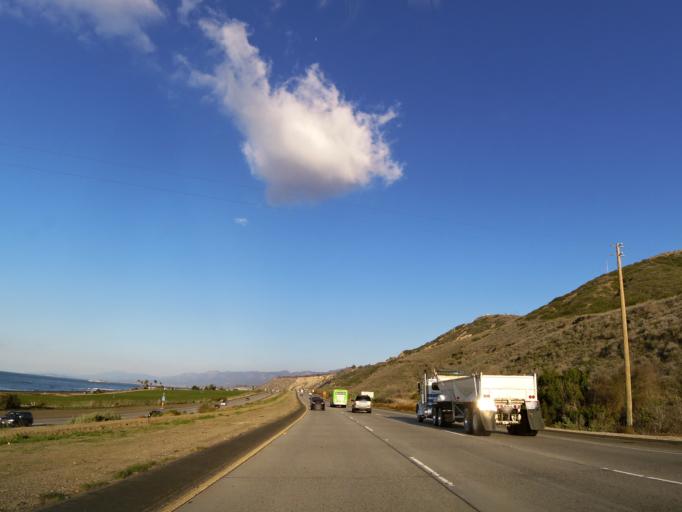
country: US
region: California
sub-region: Ventura County
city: Oak View
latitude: 34.3340
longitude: -119.4018
